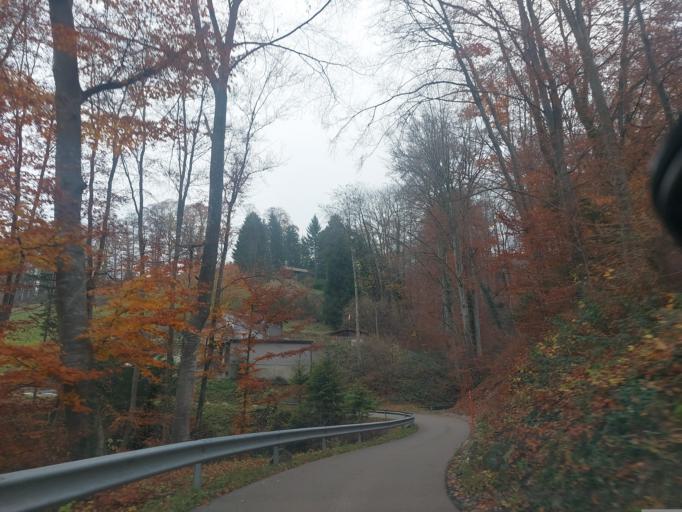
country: CH
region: Vaud
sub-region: Riviera-Pays-d'Enhaut District
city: Blonay
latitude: 46.4954
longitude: 6.8892
